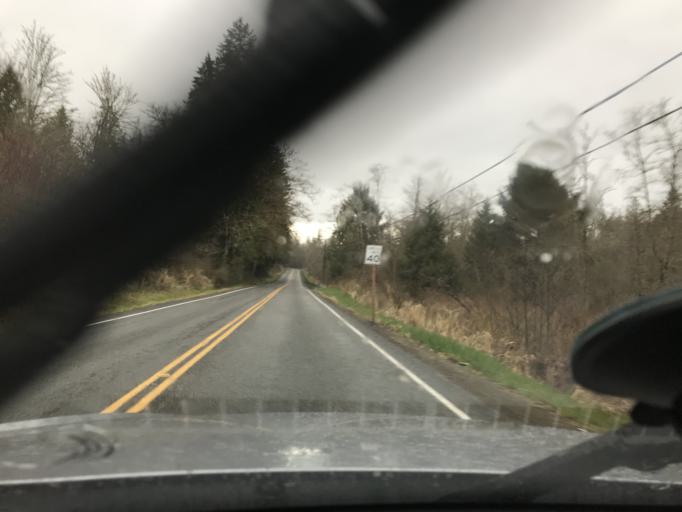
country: US
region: Washington
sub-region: King County
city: Ames Lake
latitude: 47.6528
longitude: -121.9631
